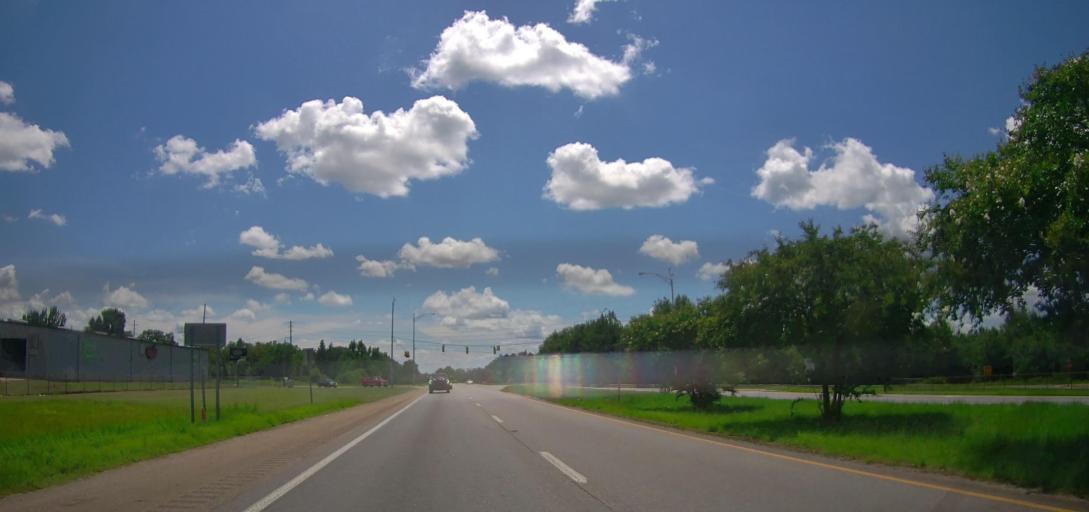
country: US
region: Alabama
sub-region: Montgomery County
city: Montgomery
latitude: 32.4116
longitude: -86.3020
